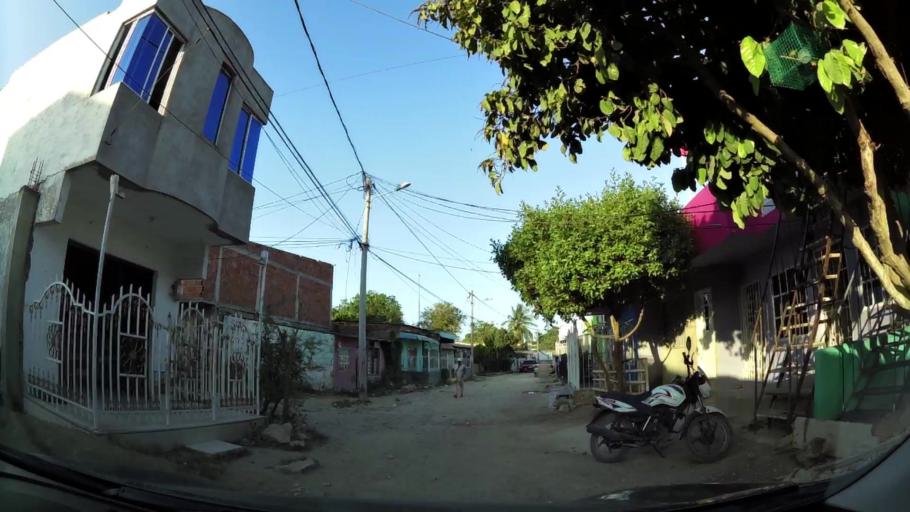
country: CO
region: Bolivar
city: Cartagena
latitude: 10.4101
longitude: -75.4547
